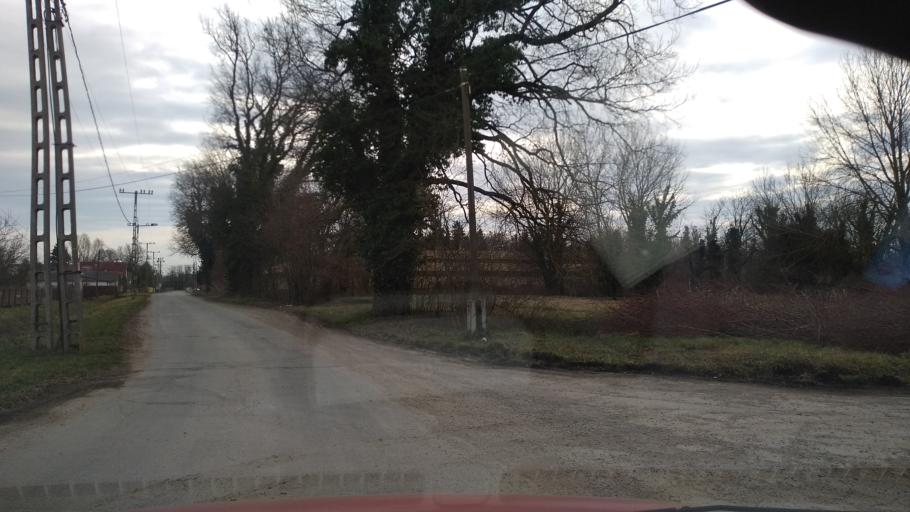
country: HU
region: Somogy
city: Barcs
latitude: 45.9570
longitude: 17.4413
